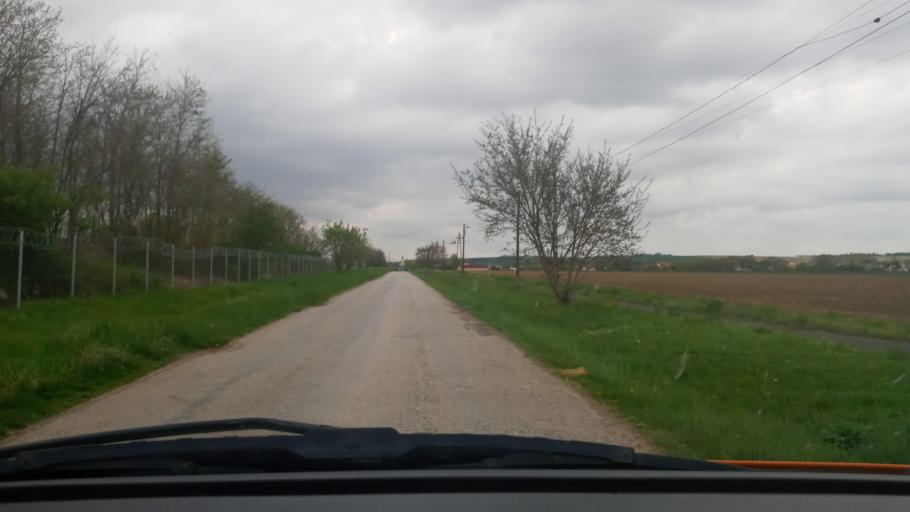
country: HU
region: Baranya
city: Boly
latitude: 45.9916
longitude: 18.5591
